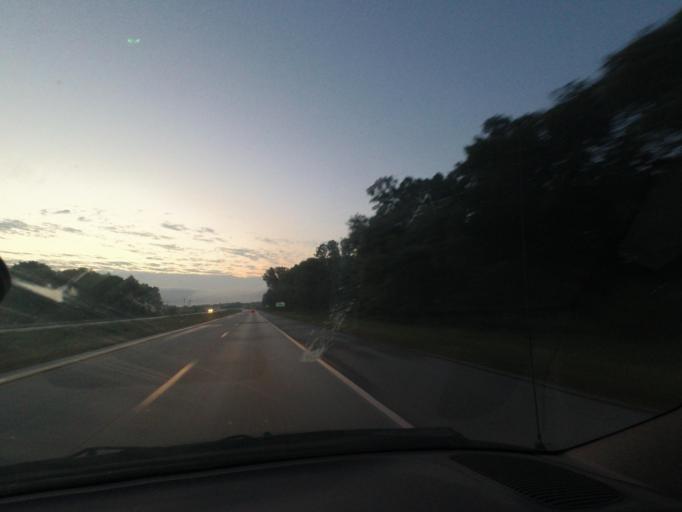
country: US
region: Missouri
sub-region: Linn County
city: Brookfield
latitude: 39.7738
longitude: -93.0851
